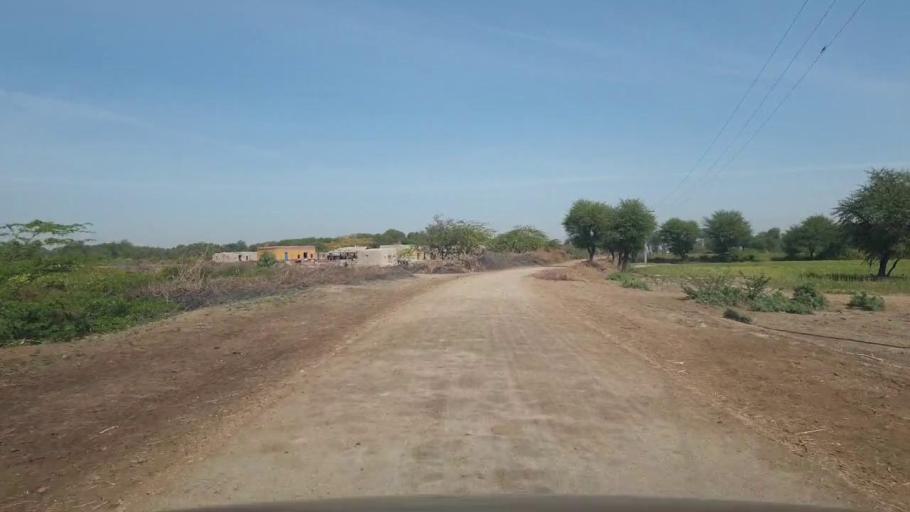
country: PK
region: Sindh
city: Umarkot
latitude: 25.3363
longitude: 69.6217
